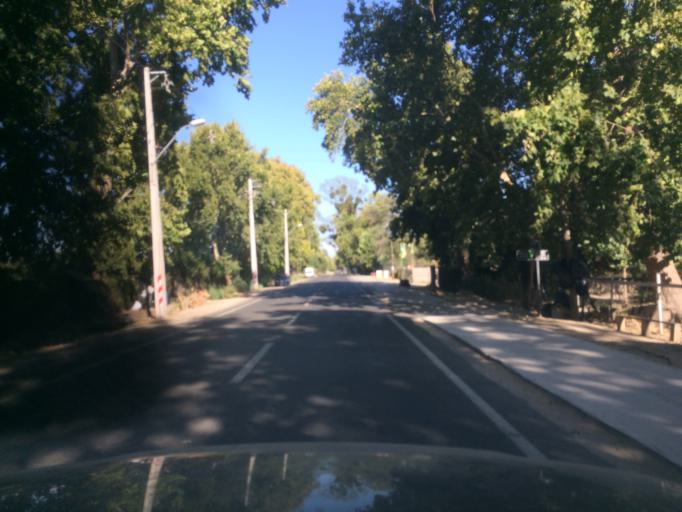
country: CL
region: Santiago Metropolitan
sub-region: Provincia de Melipilla
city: Melipilla
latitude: -33.4909
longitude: -71.1726
